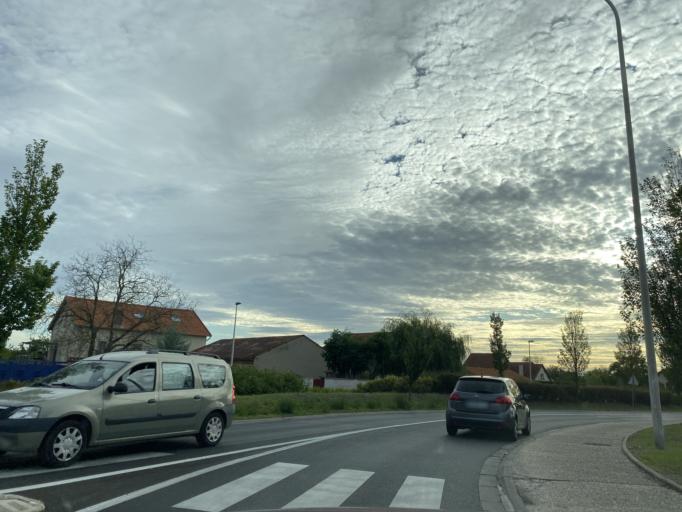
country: FR
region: Auvergne
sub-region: Departement du Puy-de-Dome
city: Lezoux
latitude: 45.8234
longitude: 3.3846
